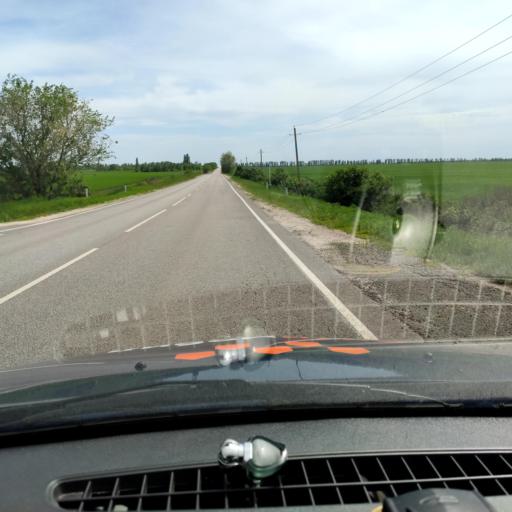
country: RU
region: Voronezj
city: Novaya Usman'
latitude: 51.5793
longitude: 39.3748
